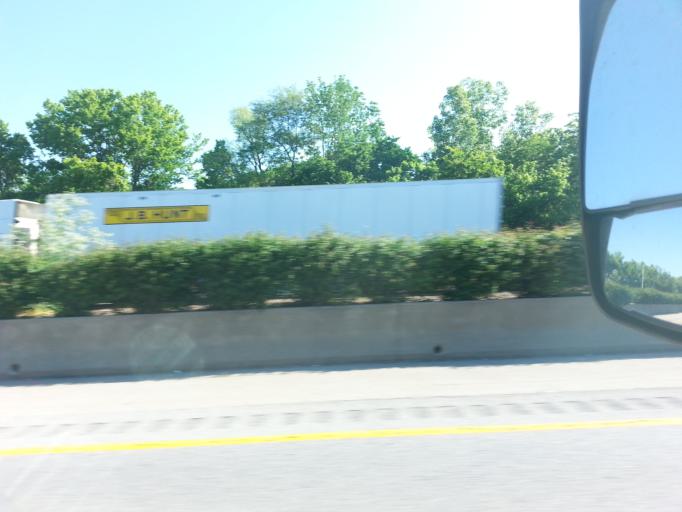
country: US
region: Kentucky
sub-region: Jefferson County
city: Hurstbourne Acres
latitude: 38.2292
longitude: -85.5976
